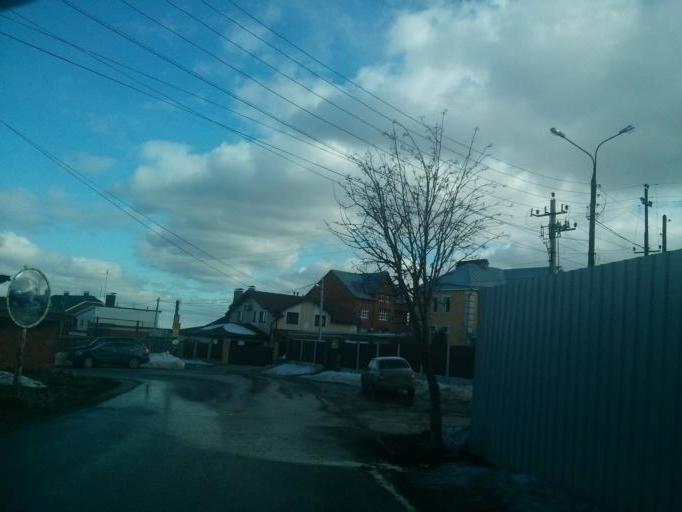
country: RU
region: Nizjnij Novgorod
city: Afonino
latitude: 56.2884
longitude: 44.0921
